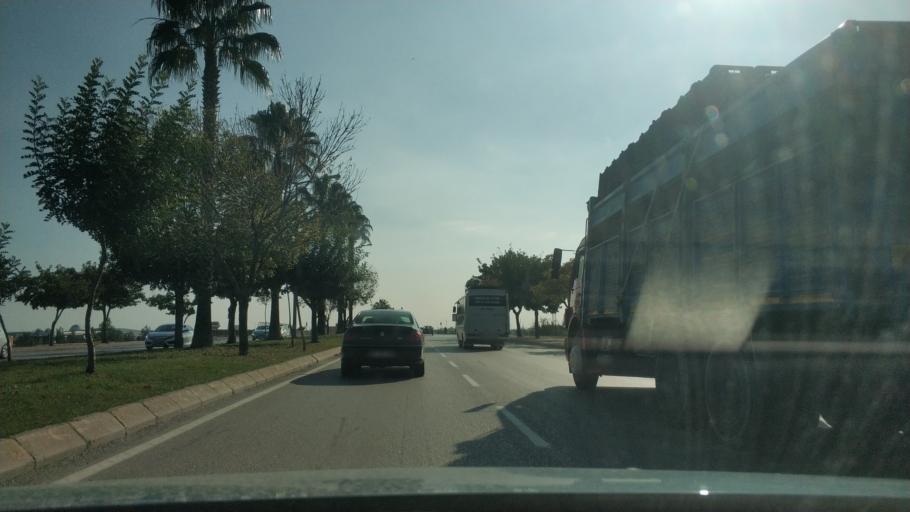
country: TR
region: Adana
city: Seyhan
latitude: 36.9997
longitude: 35.2524
